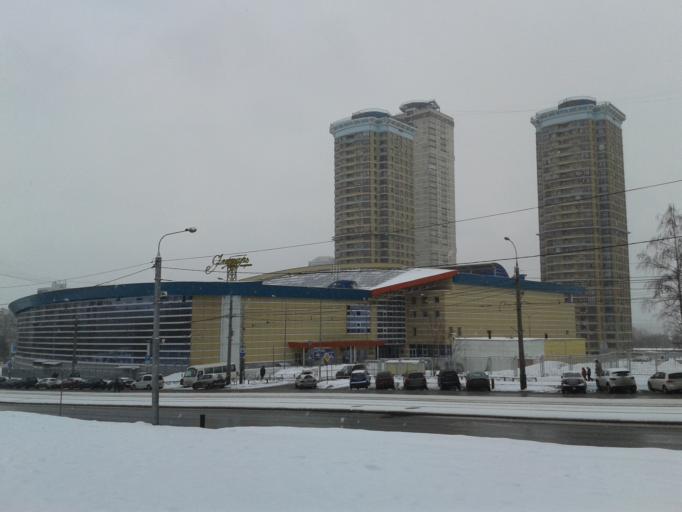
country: RU
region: Moscow
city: Strogino
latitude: 55.8038
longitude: 37.4088
